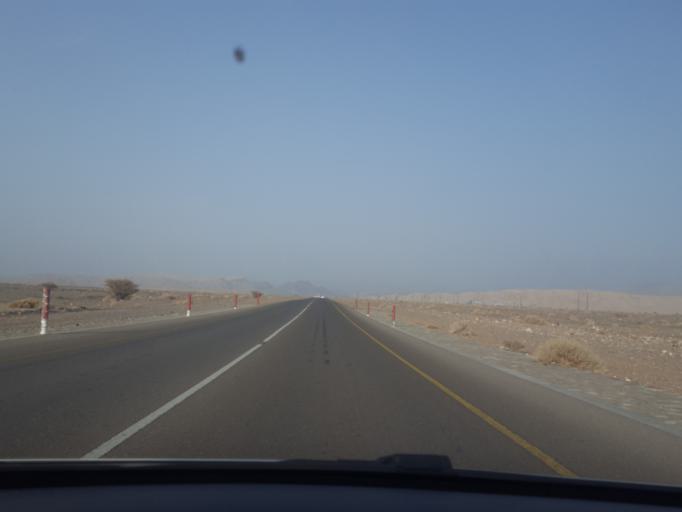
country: AE
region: Abu Dhabi
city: Al Ain
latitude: 24.0259
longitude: 55.9812
